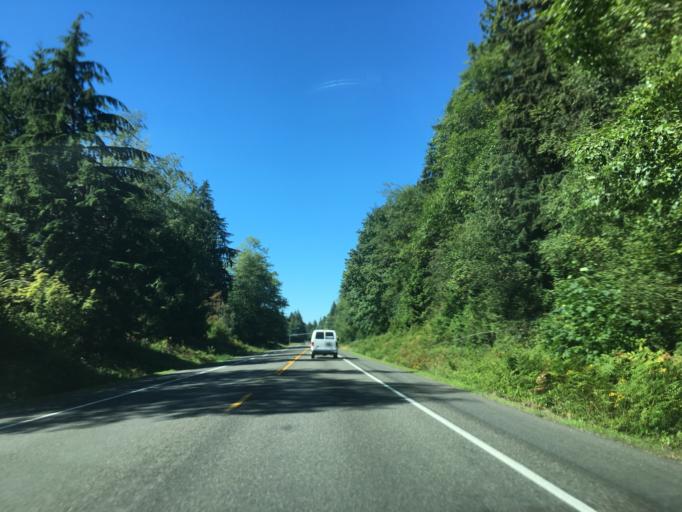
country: US
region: Washington
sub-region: Snohomish County
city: Arlington
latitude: 48.1609
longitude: -122.1171
